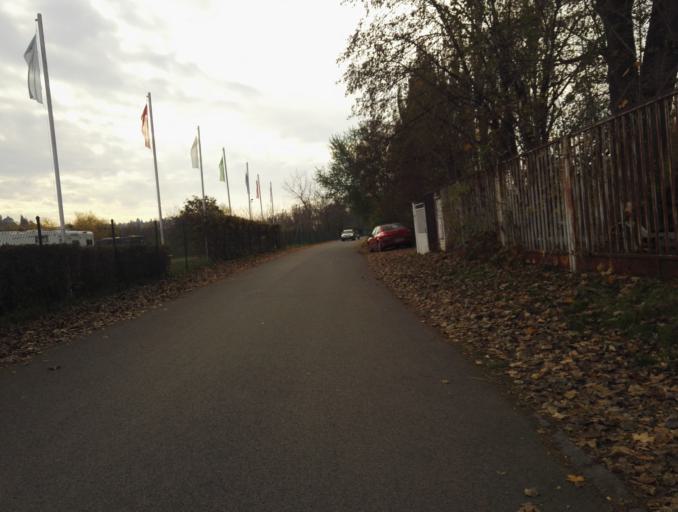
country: CZ
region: Praha
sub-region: Praha 2
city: Vysehrad
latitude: 50.0557
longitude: 14.4131
